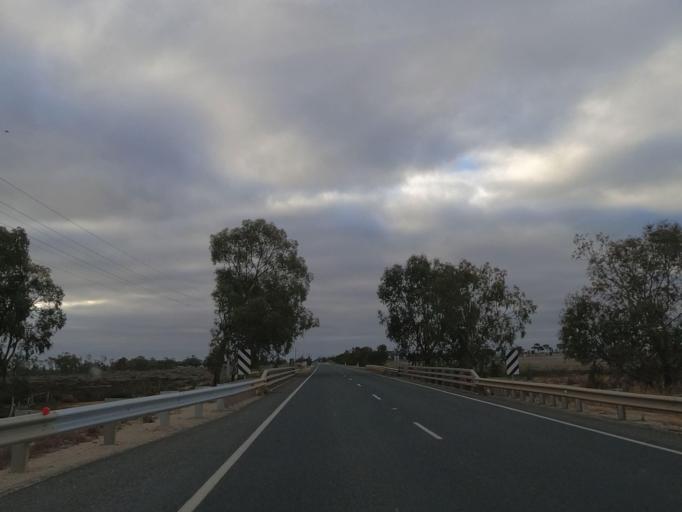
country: AU
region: Victoria
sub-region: Swan Hill
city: Swan Hill
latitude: -35.6193
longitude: 143.8034
